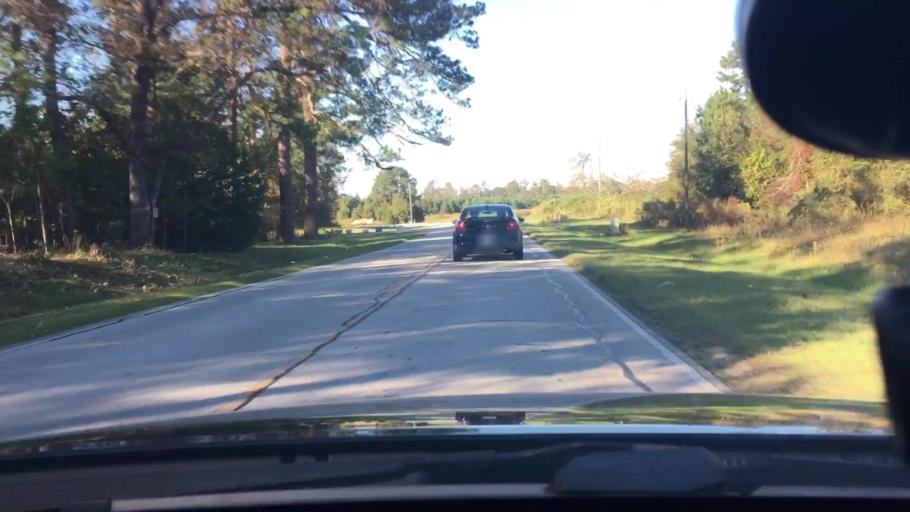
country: US
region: North Carolina
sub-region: Craven County
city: Vanceboro
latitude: 35.2787
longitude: -77.1530
